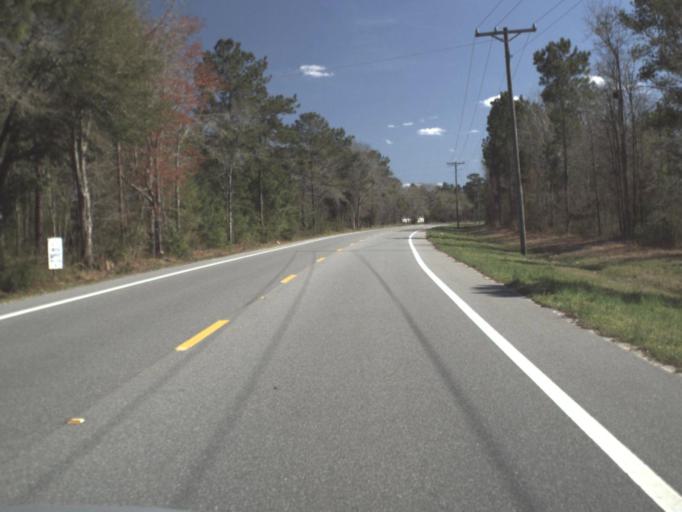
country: US
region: Florida
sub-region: Gadsden County
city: Gretna
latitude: 30.6510
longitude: -84.6829
